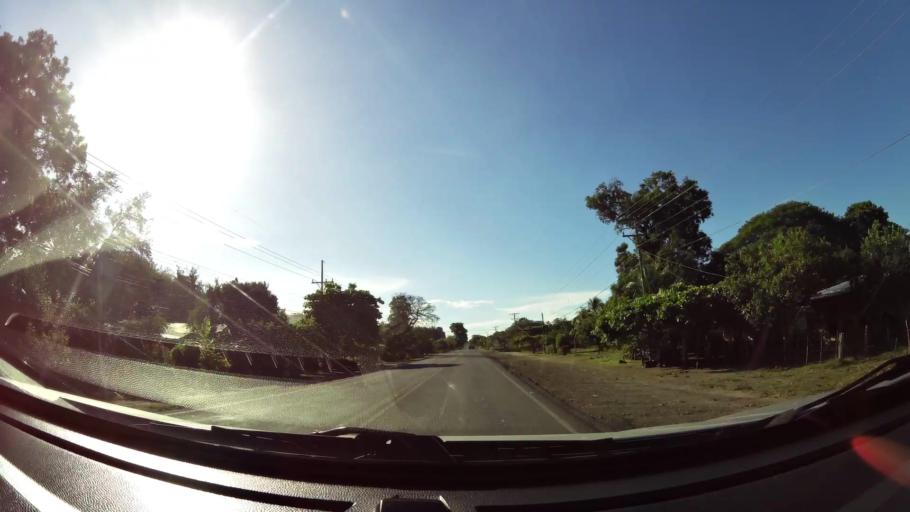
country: CR
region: Guanacaste
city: Belen
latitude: 10.4747
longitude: -85.5632
